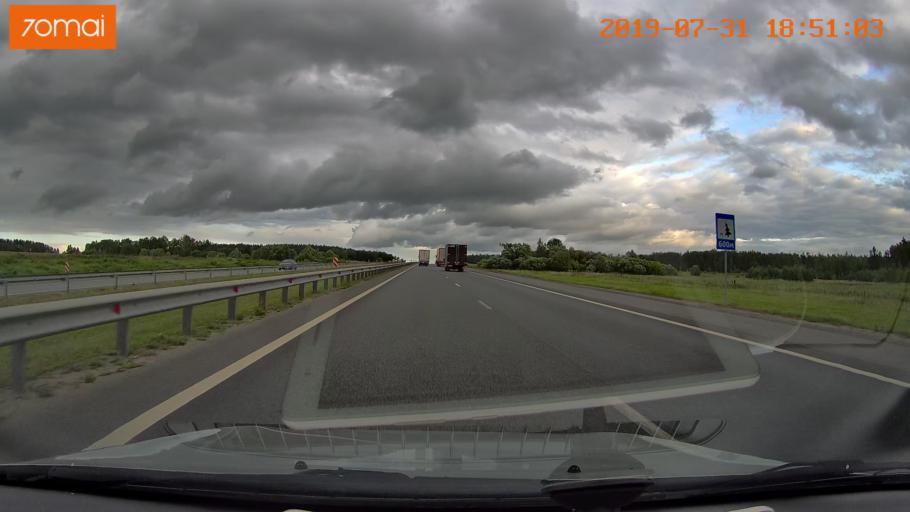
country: RU
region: Moskovskaya
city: Troitskoye
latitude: 55.2246
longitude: 38.5971
